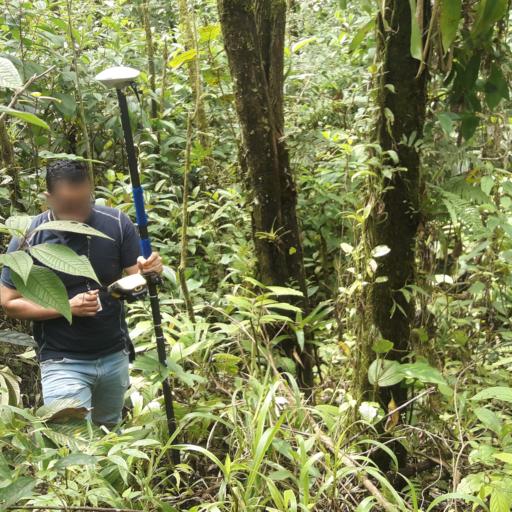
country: EC
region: Napo
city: Archidona
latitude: -0.9483
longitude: -77.8623
